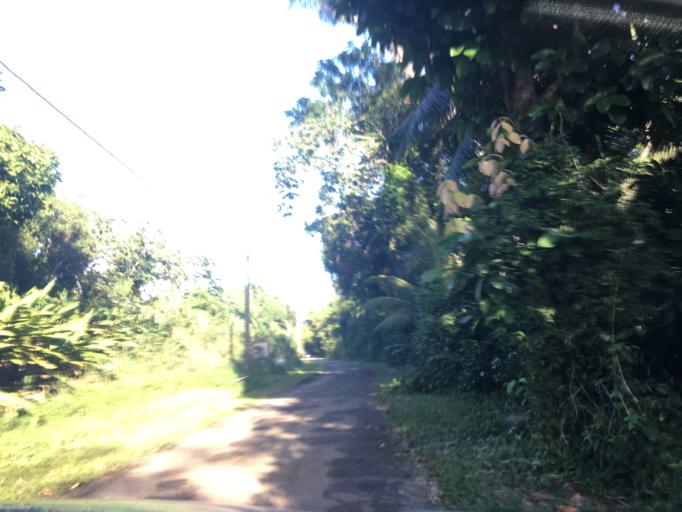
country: BZ
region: Stann Creek
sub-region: Dangriga
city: Dangriga
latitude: 16.8232
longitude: -88.3169
